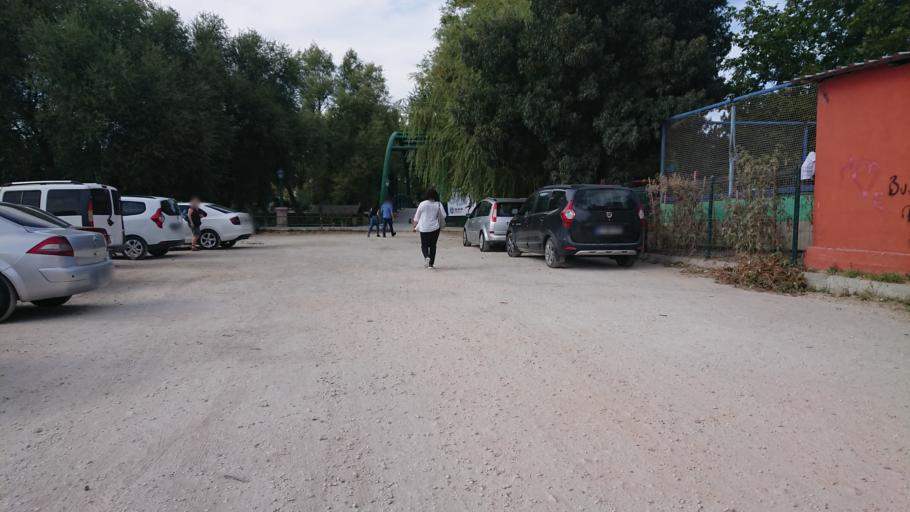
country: TR
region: Eskisehir
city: Eskisehir
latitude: 39.7685
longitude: 30.4961
